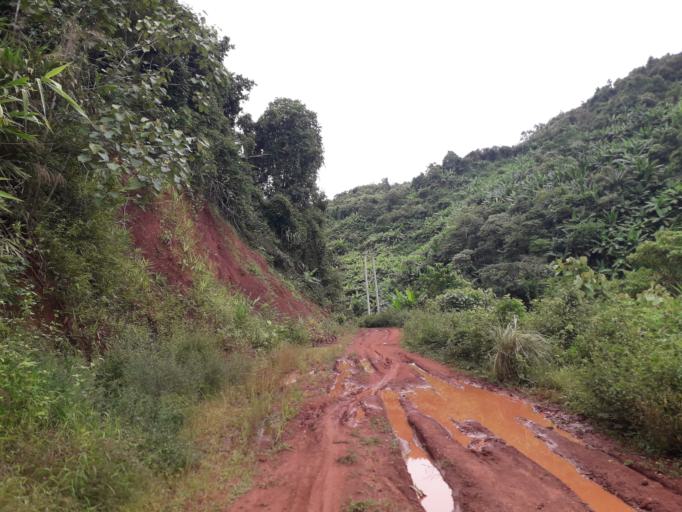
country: CN
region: Yunnan
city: Menglie
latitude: 22.1911
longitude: 101.7061
